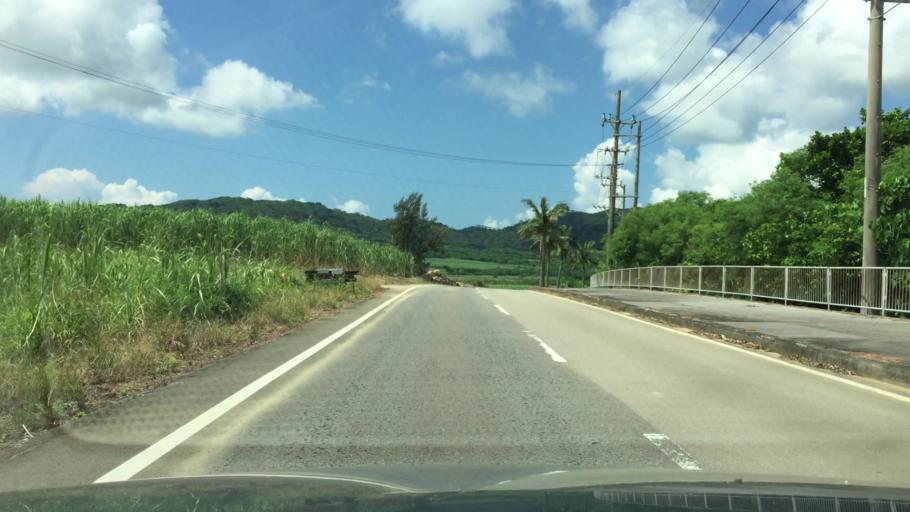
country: JP
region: Okinawa
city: Ishigaki
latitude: 24.3936
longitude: 124.1527
